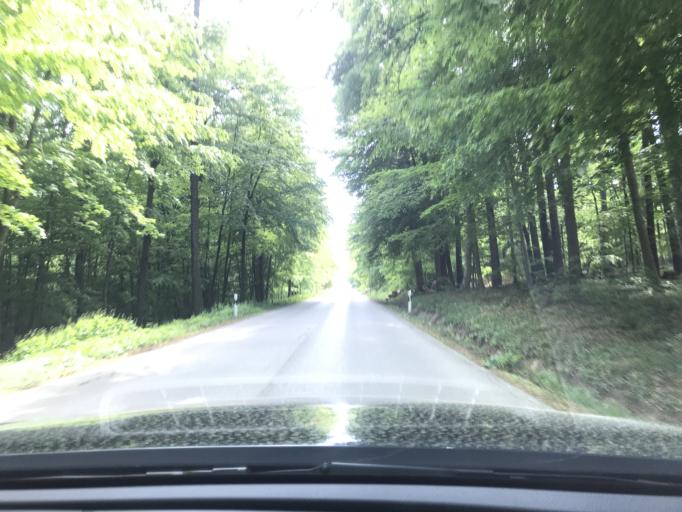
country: DE
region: Baden-Wuerttemberg
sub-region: Regierungsbezirk Stuttgart
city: Weinstadt-Endersbach
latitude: 48.7703
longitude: 9.3730
